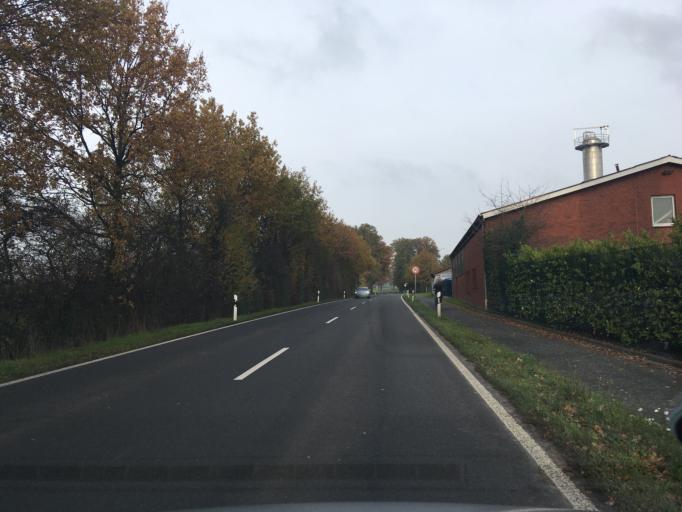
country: DE
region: North Rhine-Westphalia
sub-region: Regierungsbezirk Munster
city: Velen
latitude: 51.8975
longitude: 6.9745
